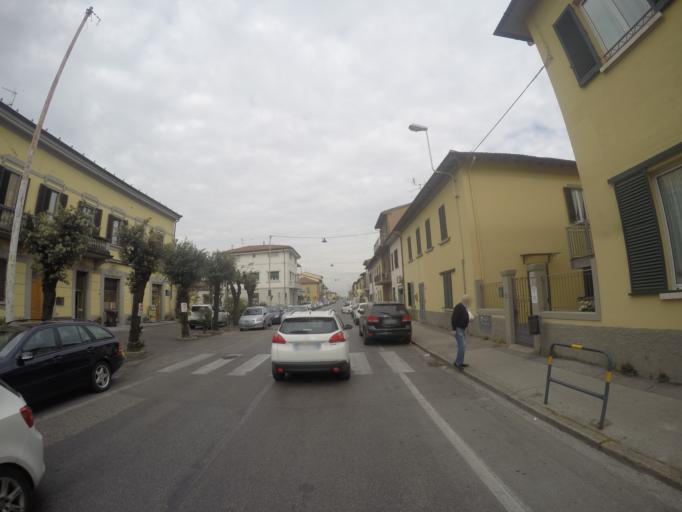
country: IT
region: Tuscany
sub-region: Provincia di Prato
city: Prato
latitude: 43.8957
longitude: 11.0638
